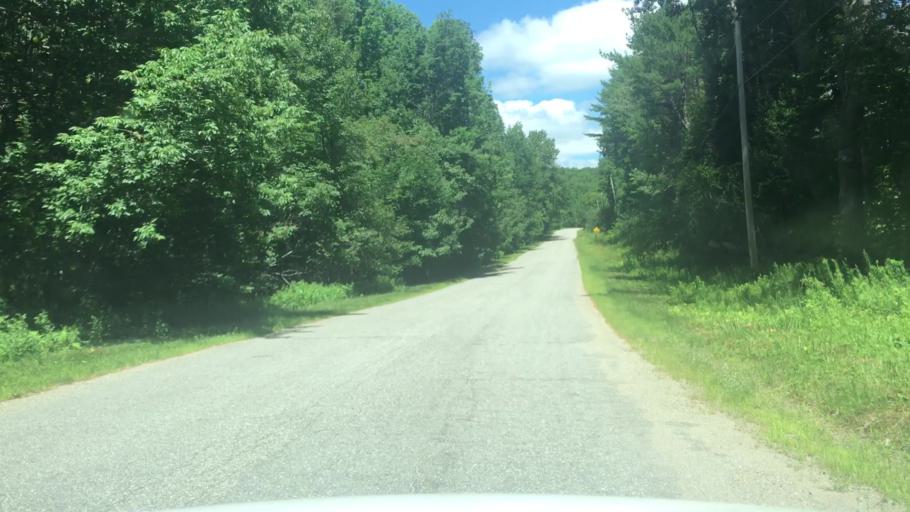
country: US
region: Maine
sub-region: Kennebec County
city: Albion
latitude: 44.4771
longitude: -69.3001
